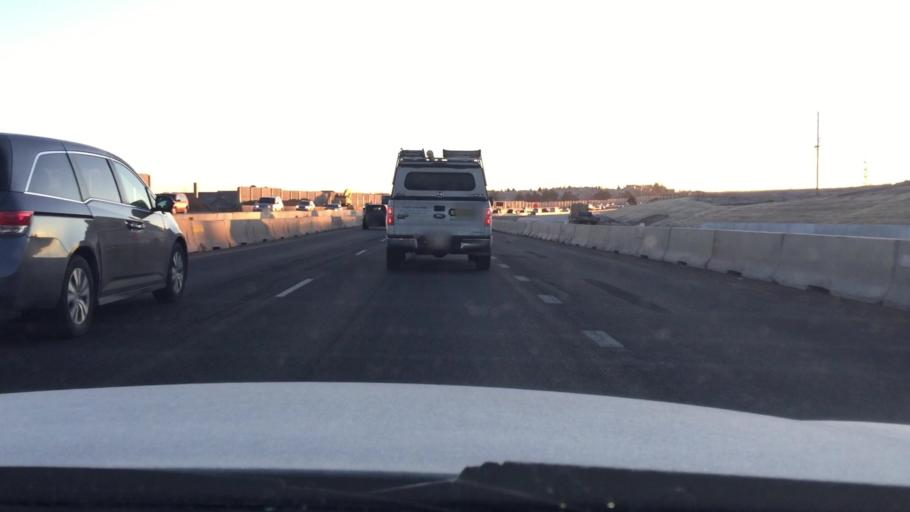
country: US
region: Colorado
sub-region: Douglas County
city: Highlands Ranch
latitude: 39.5635
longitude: -104.9532
